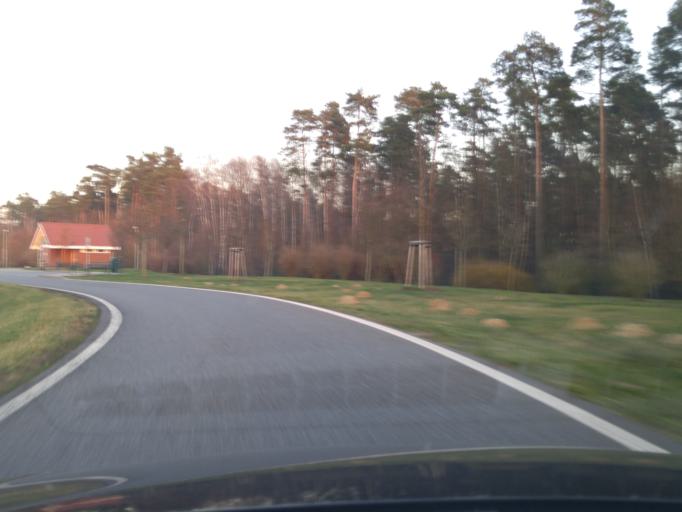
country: DE
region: Berlin
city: Wannsee
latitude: 52.3833
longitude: 13.1530
